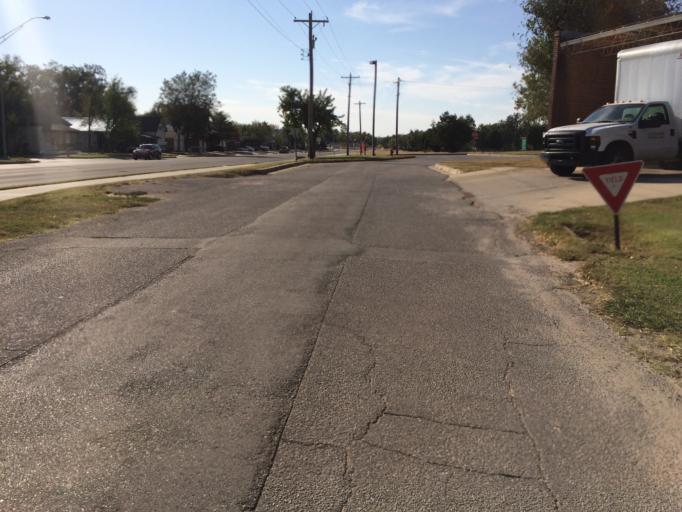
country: US
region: Oklahoma
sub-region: Cleveland County
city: Norman
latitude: 35.2258
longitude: -97.4285
